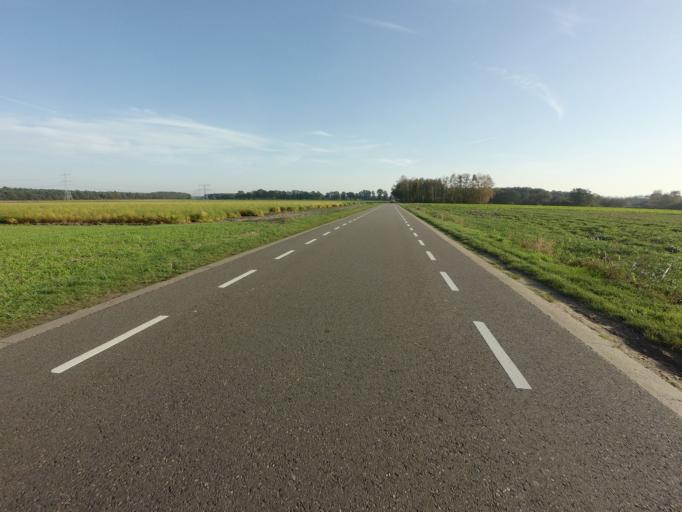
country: NL
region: Limburg
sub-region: Gemeente Roerdalen
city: Montfort
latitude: 51.1128
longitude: 5.9747
